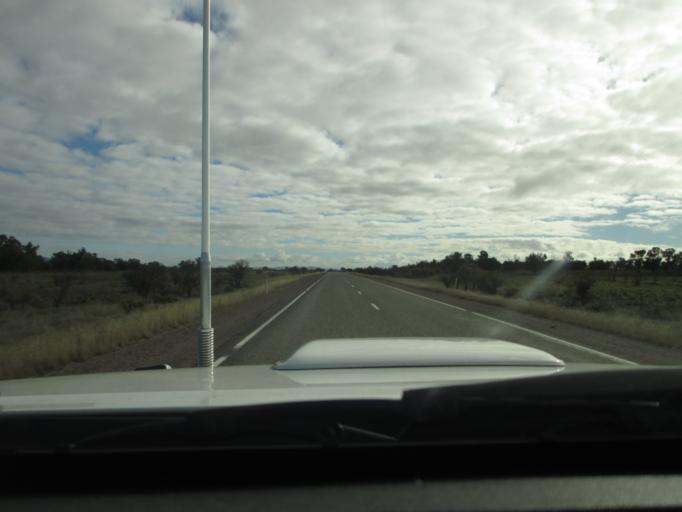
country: AU
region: South Australia
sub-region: Flinders Ranges
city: Quorn
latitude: -32.4669
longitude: 138.5389
